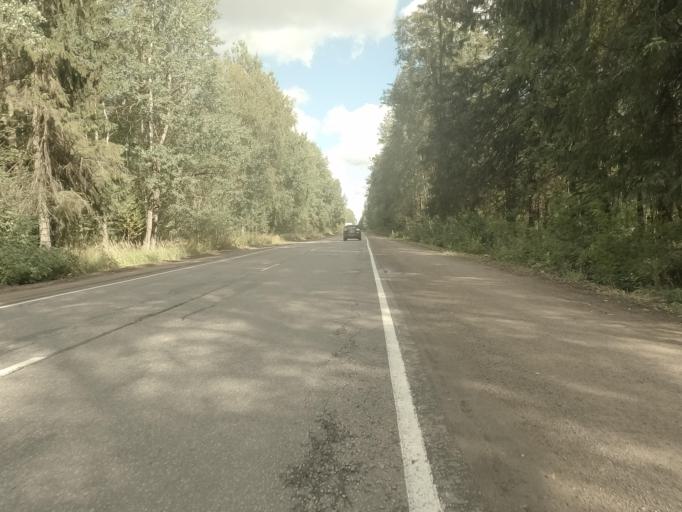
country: RU
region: Leningrad
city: Romanovka
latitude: 60.0220
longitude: 30.7193
